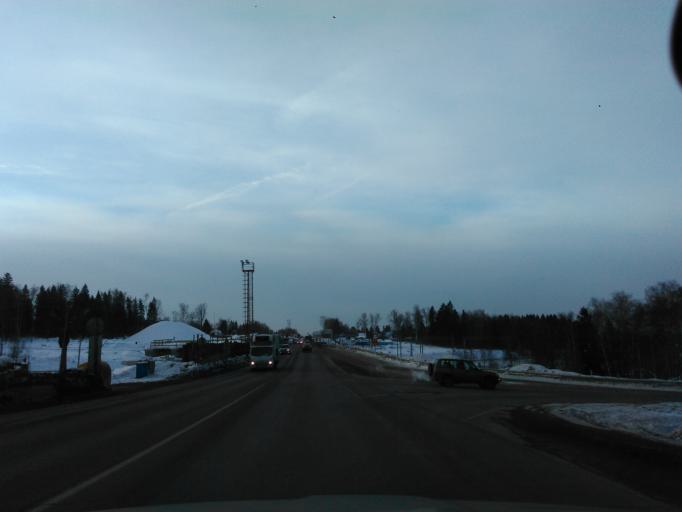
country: RU
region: Moskovskaya
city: Istra
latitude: 55.8957
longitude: 36.9445
